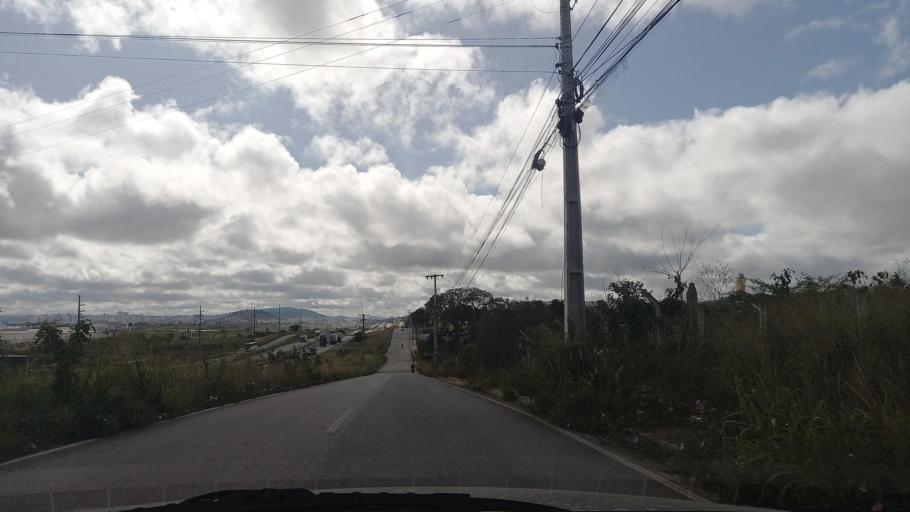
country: BR
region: Pernambuco
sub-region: Caruaru
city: Caruaru
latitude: -8.3074
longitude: -36.0189
